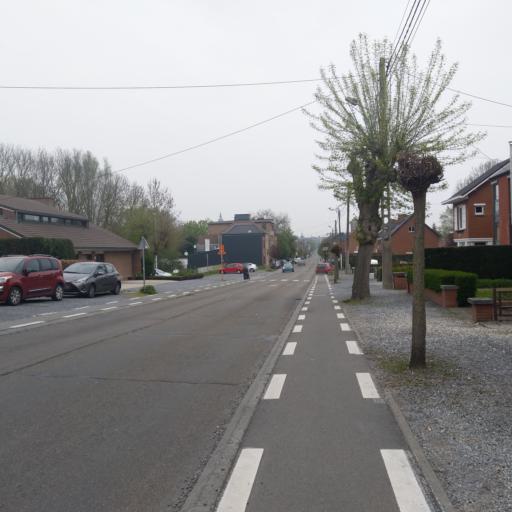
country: BE
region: Wallonia
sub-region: Province du Hainaut
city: Mons
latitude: 50.4421
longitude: 3.9556
